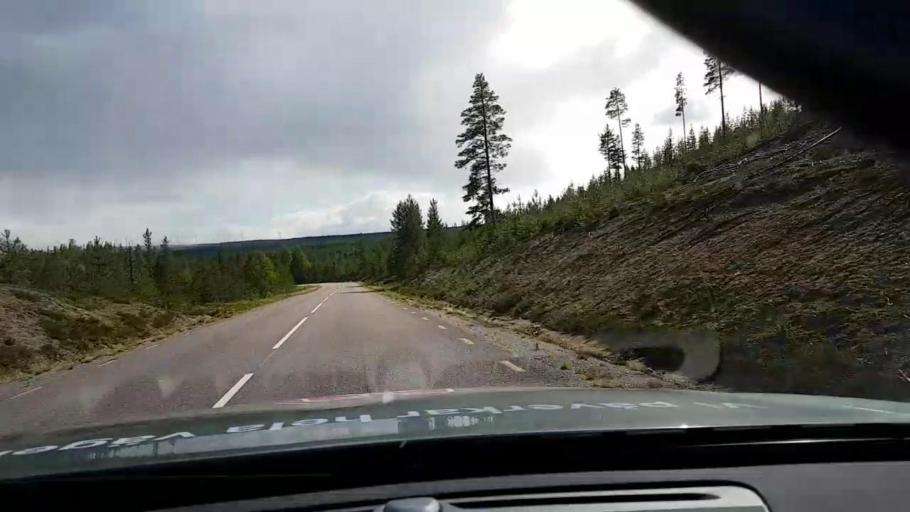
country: SE
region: Vaesterbotten
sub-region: Asele Kommun
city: Asele
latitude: 63.8732
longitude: 17.3568
